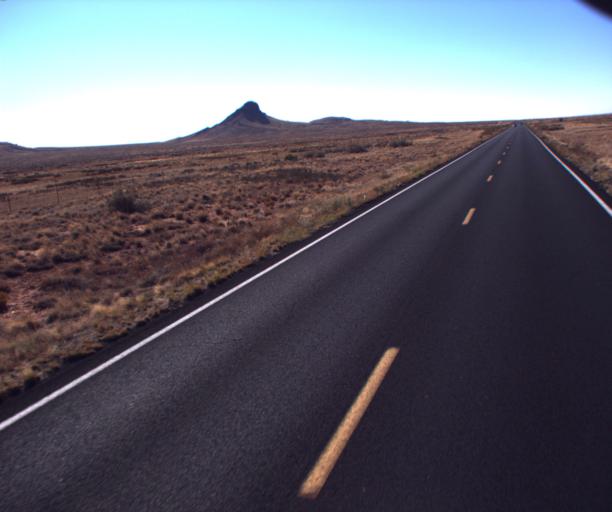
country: US
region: Arizona
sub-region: Navajo County
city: Dilkon
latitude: 35.4364
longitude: -110.4249
